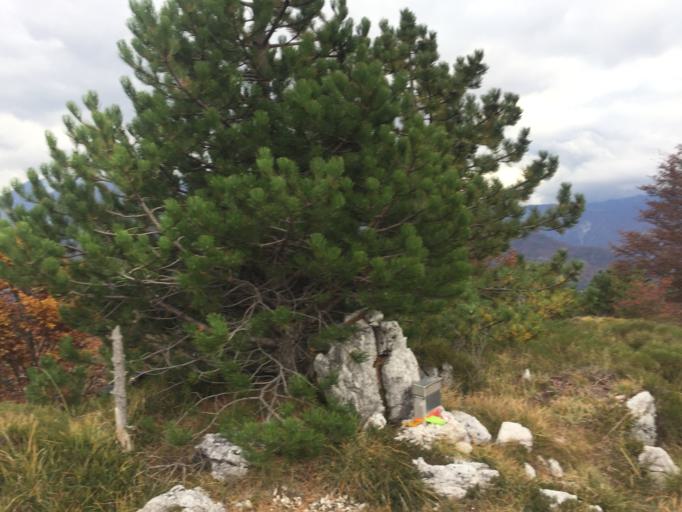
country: IT
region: Friuli Venezia Giulia
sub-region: Provincia di Udine
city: Chiusaforte
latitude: 46.4179
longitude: 13.3006
